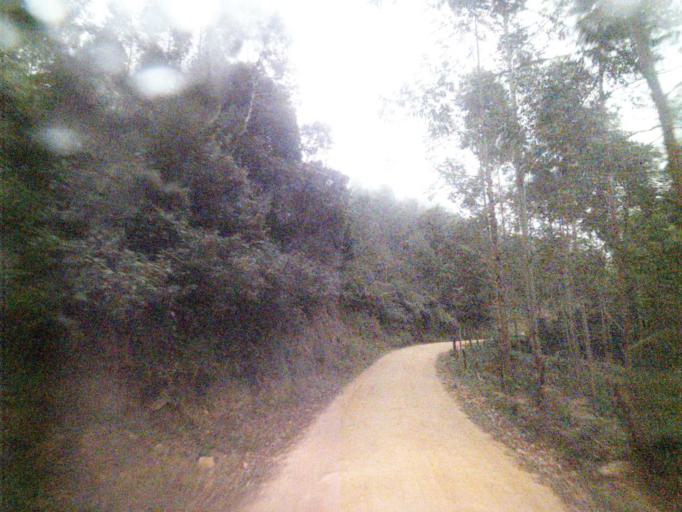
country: BR
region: Santa Catarina
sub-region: Anitapolis
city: Anitapolis
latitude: -27.8195
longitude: -49.1356
